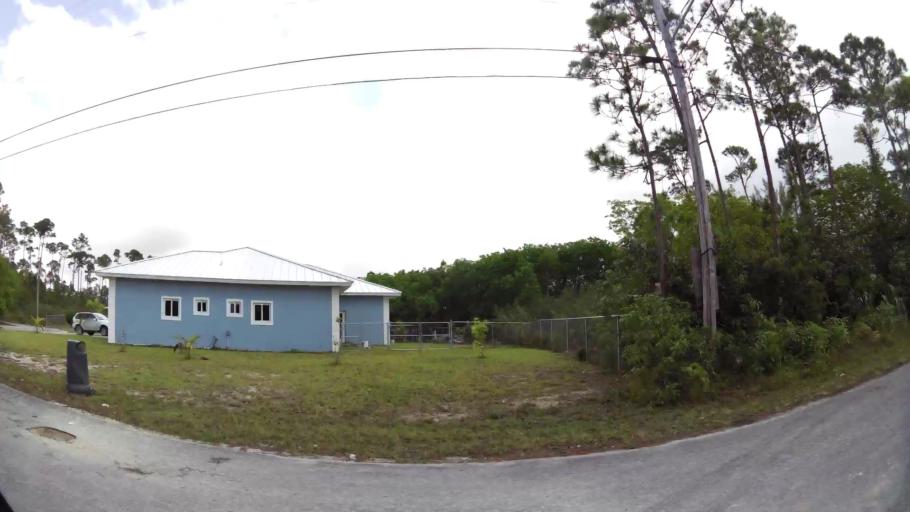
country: BS
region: Freeport
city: Lucaya
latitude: 26.5443
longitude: -78.5915
